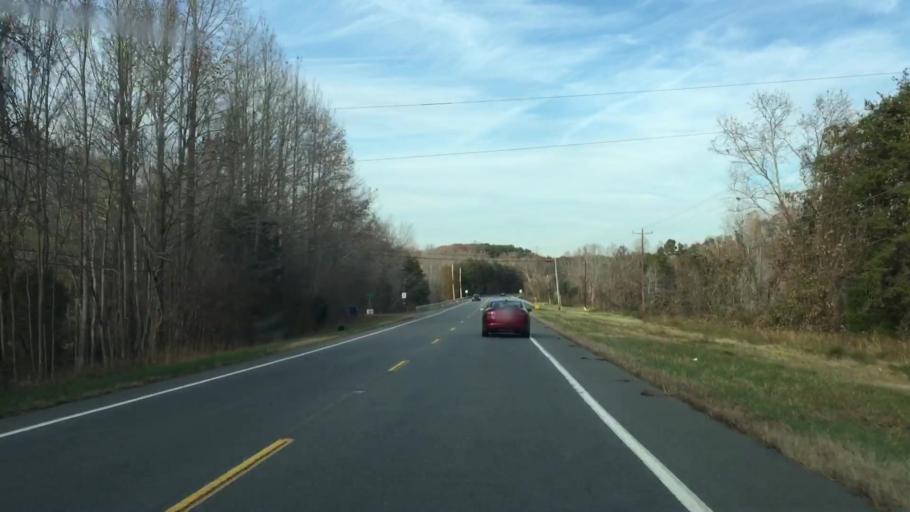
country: US
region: North Carolina
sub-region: Rockingham County
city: Reidsville
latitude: 36.3039
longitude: -79.7222
